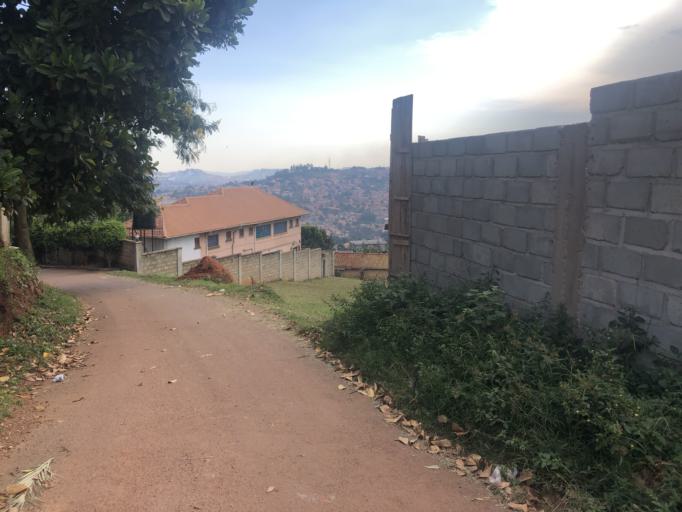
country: UG
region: Central Region
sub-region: Kampala District
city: Kampala
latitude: 0.2754
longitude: 32.5901
